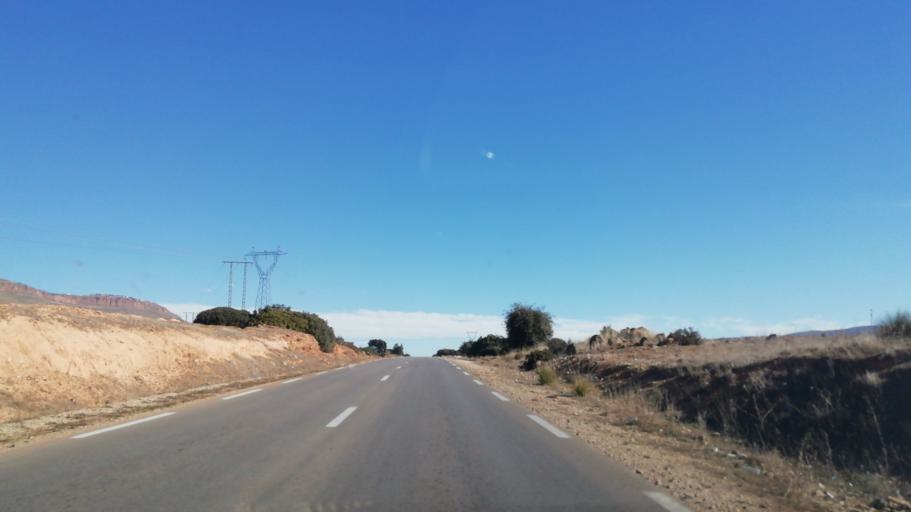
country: DZ
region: Tlemcen
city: Sebdou
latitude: 34.7129
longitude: -1.2087
